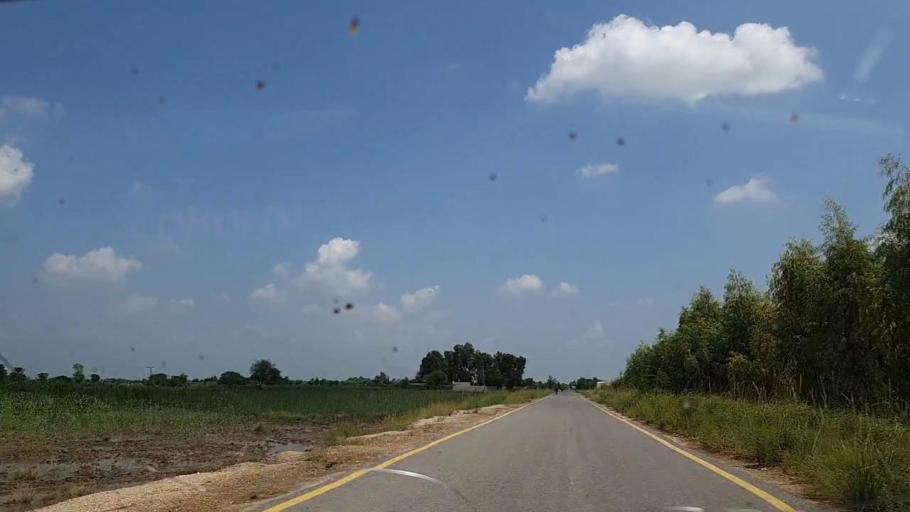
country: PK
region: Sindh
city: Tharu Shah
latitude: 26.9739
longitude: 68.0885
